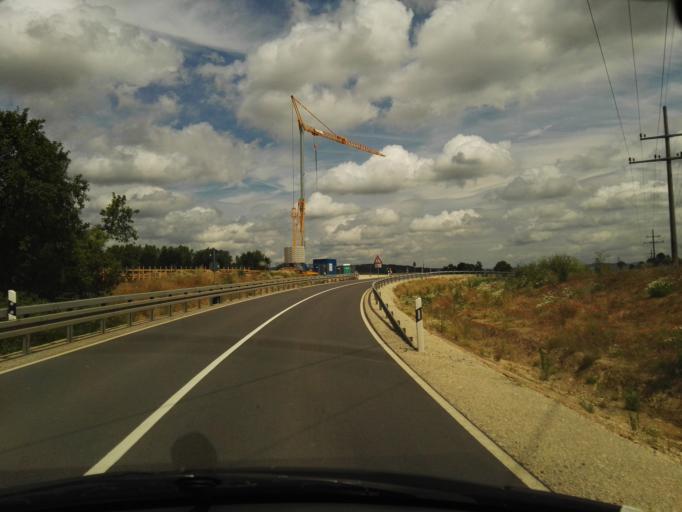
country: DE
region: Bavaria
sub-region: Upper Franconia
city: Redwitz an der Rodach
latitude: 50.1639
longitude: 11.1973
